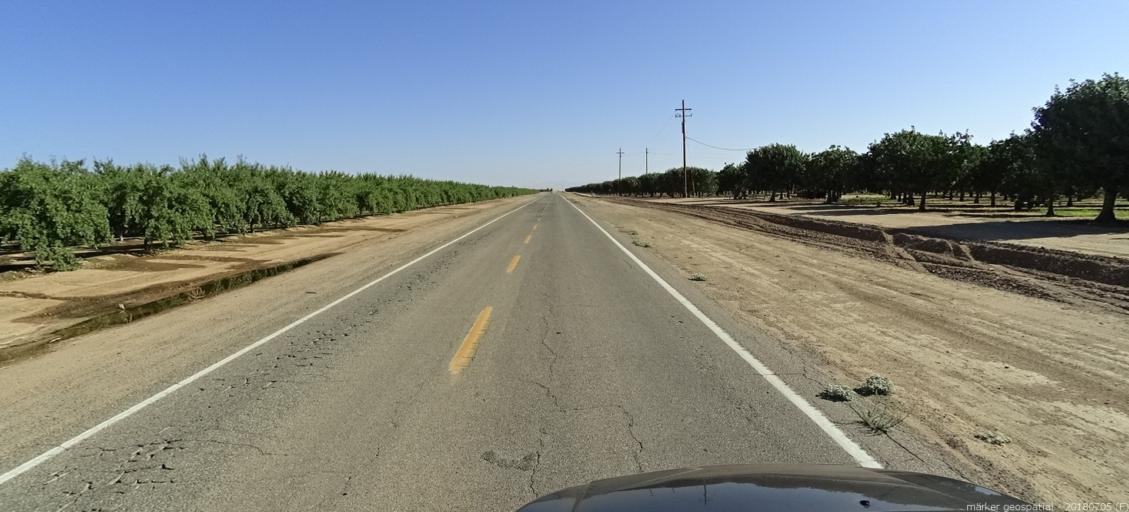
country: US
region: California
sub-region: Madera County
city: Madera Acres
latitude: 37.1033
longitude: -120.0746
